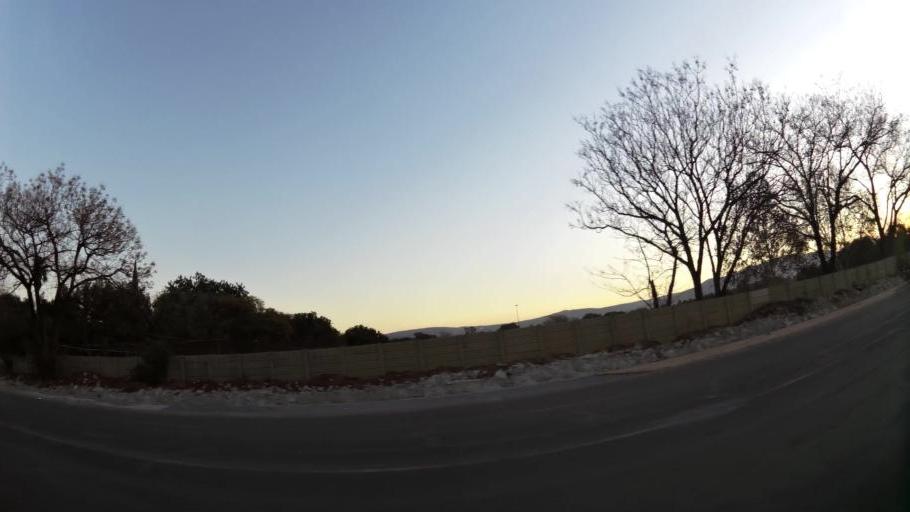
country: ZA
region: North-West
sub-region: Bojanala Platinum District Municipality
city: Rustenburg
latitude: -25.6560
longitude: 27.2419
